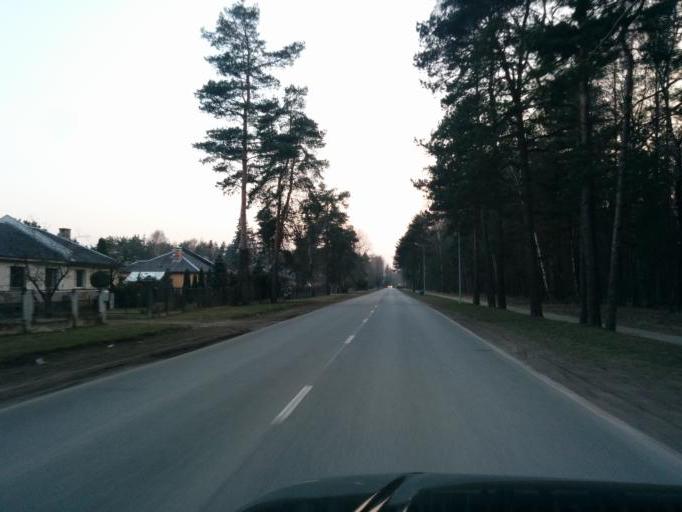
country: LV
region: Kekava
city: Balozi
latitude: 56.8733
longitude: 24.1148
